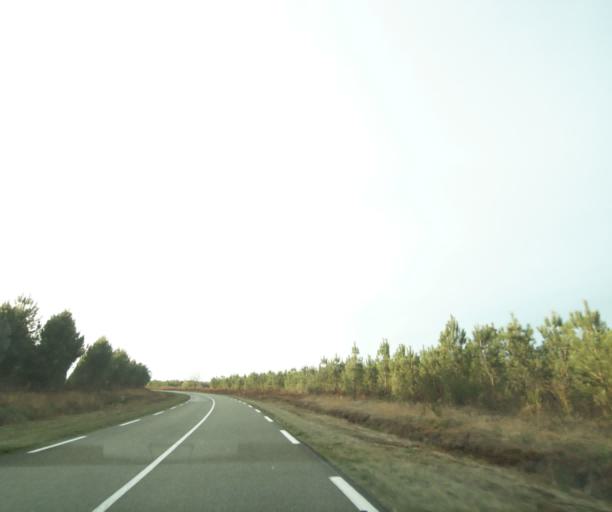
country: FR
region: Aquitaine
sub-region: Departement des Landes
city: Gabarret
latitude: 44.0869
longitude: -0.0776
